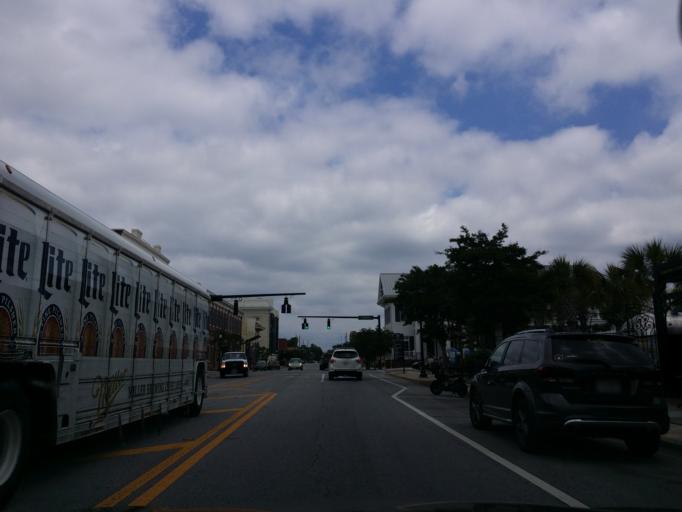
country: US
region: Florida
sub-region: Escambia County
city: Pensacola
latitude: 30.4075
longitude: -87.2148
